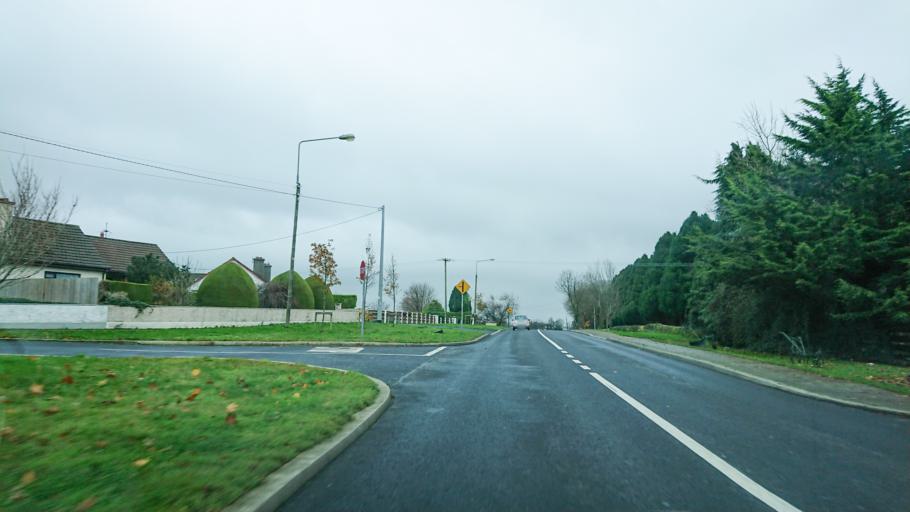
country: IE
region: Leinster
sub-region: Kilkenny
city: Mooncoin
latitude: 52.2971
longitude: -7.2630
